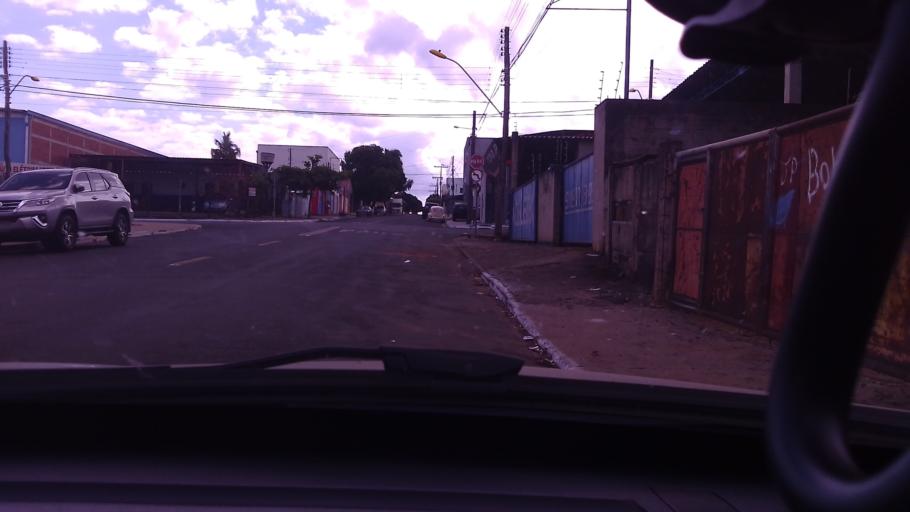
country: BR
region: Goias
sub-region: Mineiros
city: Mineiros
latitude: -17.5622
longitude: -52.5509
